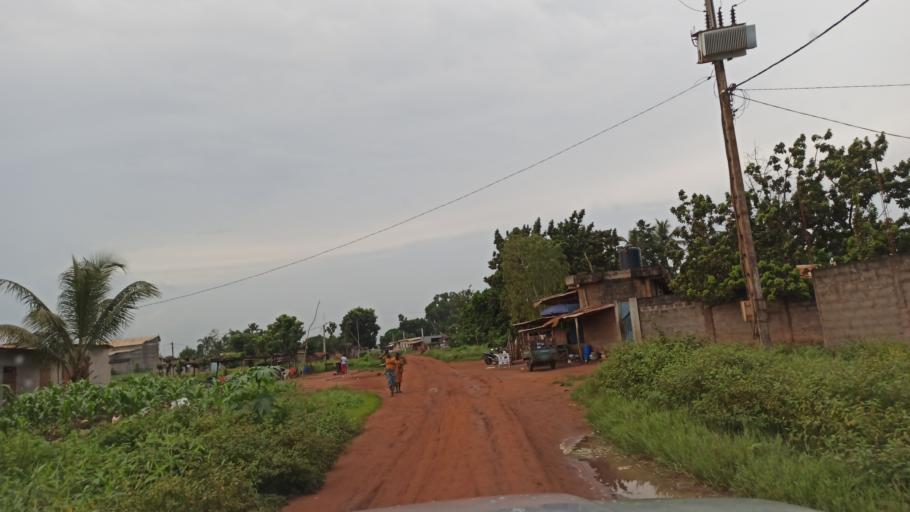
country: BJ
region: Queme
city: Porto-Novo
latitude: 6.4791
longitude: 2.6741
